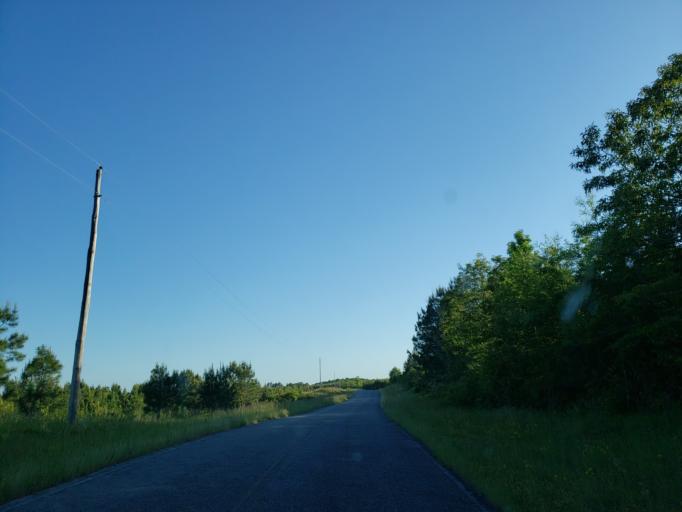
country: US
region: Georgia
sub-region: Haralson County
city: Tallapoosa
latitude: 33.7838
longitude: -85.3212
